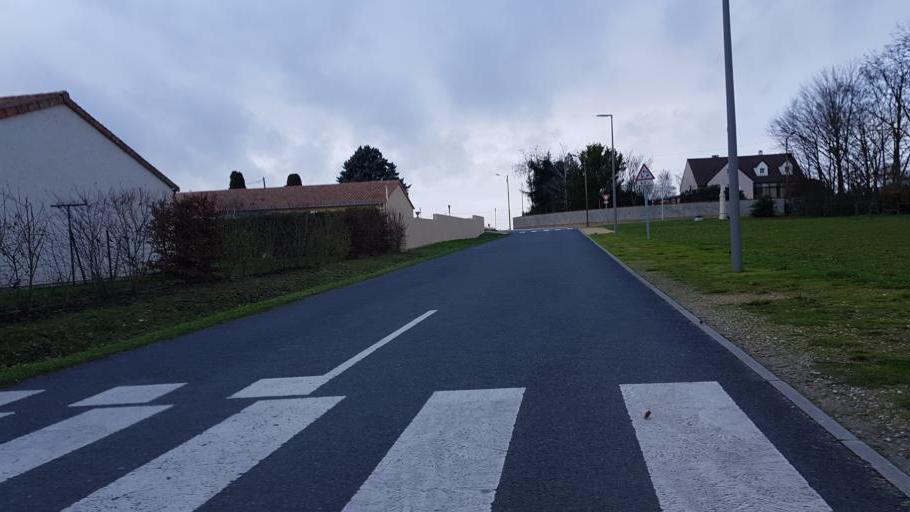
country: FR
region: Poitou-Charentes
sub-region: Departement de la Vienne
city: Avanton
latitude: 46.6631
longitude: 0.3086
